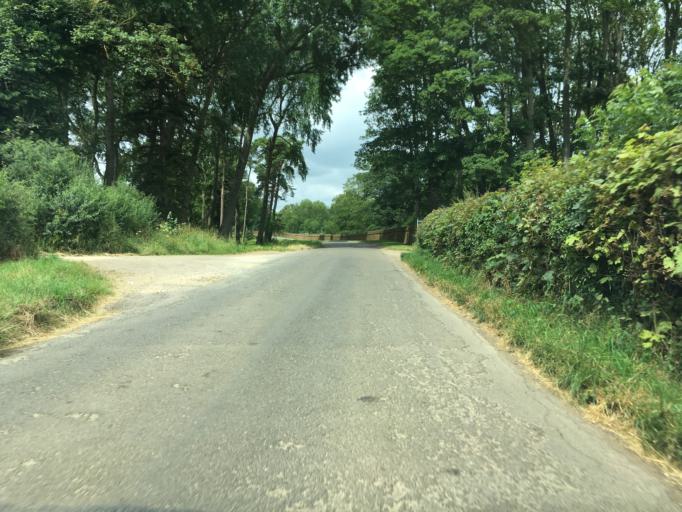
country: GB
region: England
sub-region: Oxfordshire
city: Bloxham
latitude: 51.9536
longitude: -1.4090
